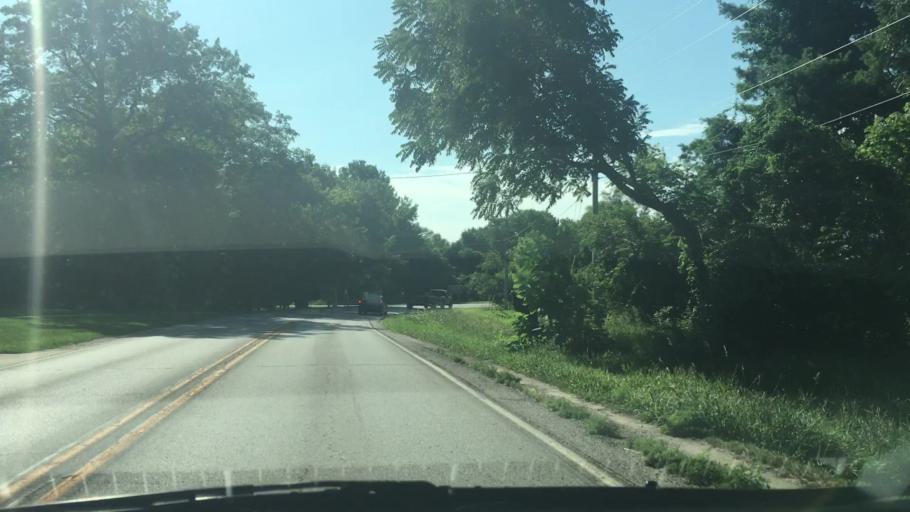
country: US
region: Iowa
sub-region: Johnson County
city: Coralville
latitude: 41.7200
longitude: -91.5551
